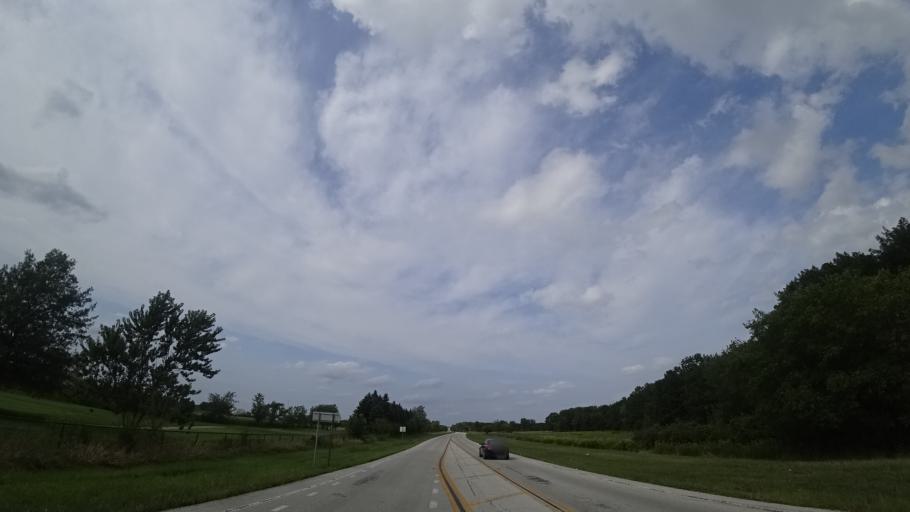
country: US
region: Illinois
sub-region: Will County
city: Frankfort Square
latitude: 41.5292
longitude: -87.7711
